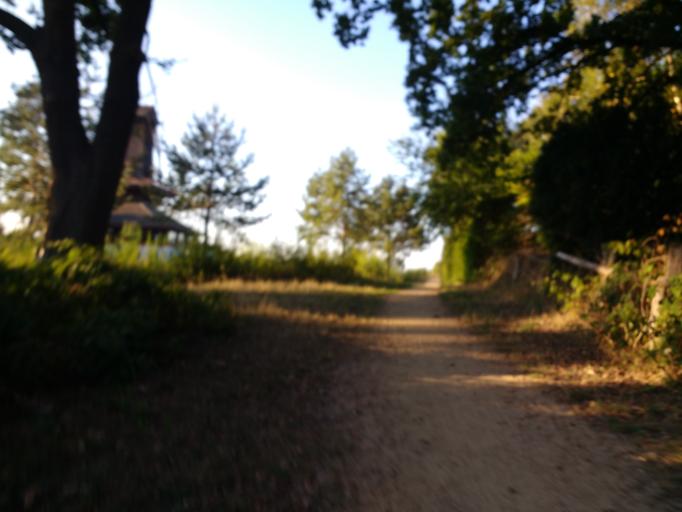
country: DE
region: Lower Saxony
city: Gifhorn
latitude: 52.4919
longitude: 10.5553
